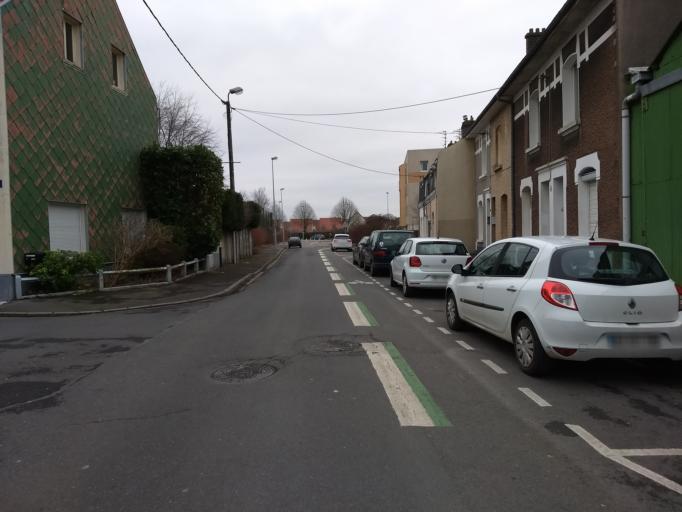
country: FR
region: Nord-Pas-de-Calais
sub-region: Departement du Pas-de-Calais
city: Arras
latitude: 50.2862
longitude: 2.7948
